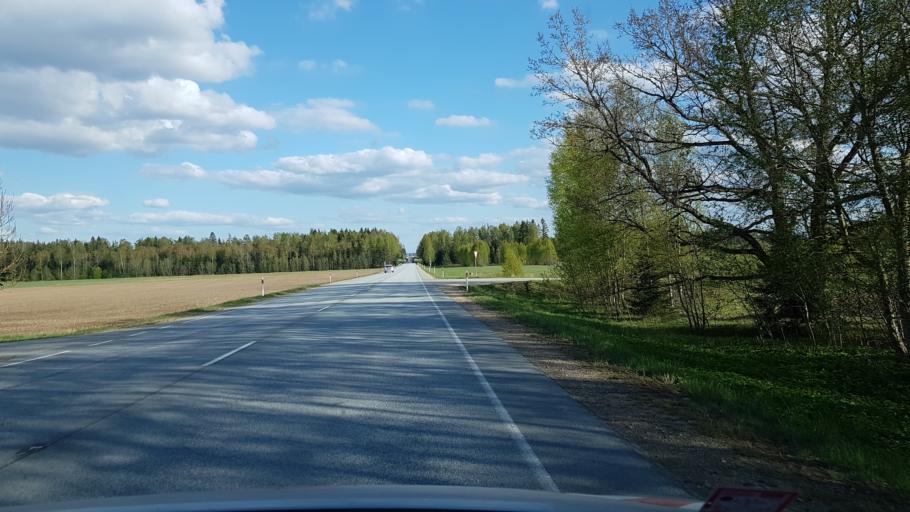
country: EE
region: Vorumaa
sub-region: Voru linn
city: Voru
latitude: 57.9042
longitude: 26.8337
